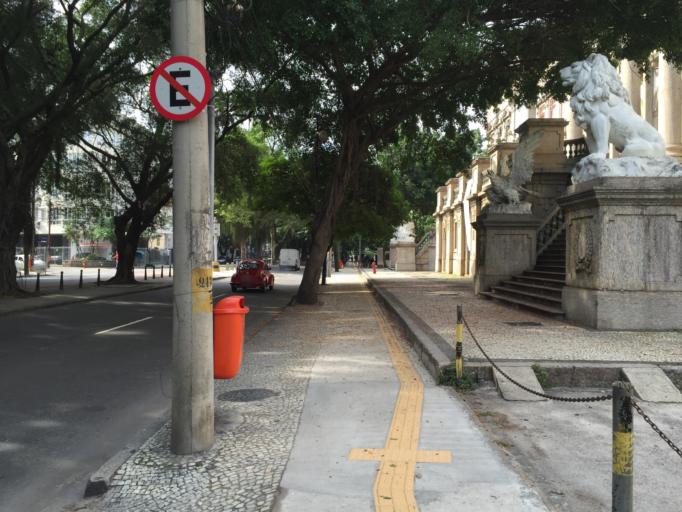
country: BR
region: Rio de Janeiro
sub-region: Rio De Janeiro
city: Rio de Janeiro
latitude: -22.9537
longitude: -43.1706
